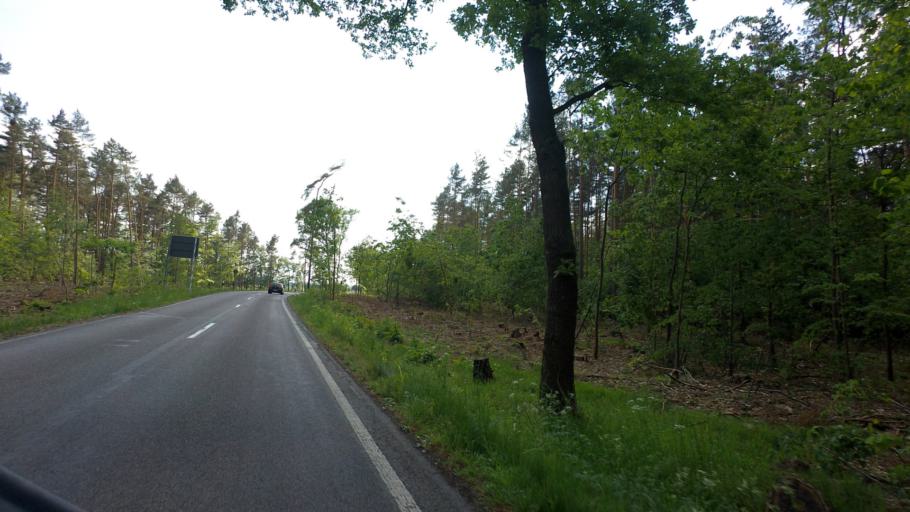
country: DE
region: Saxony
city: Mucka
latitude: 51.2821
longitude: 14.6558
